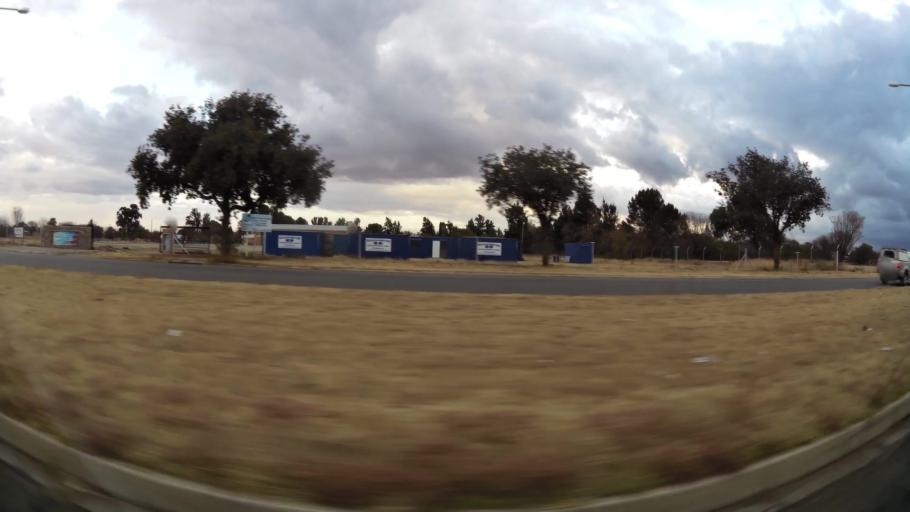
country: ZA
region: Orange Free State
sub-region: Lejweleputswa District Municipality
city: Welkom
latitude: -27.9729
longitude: 26.7579
